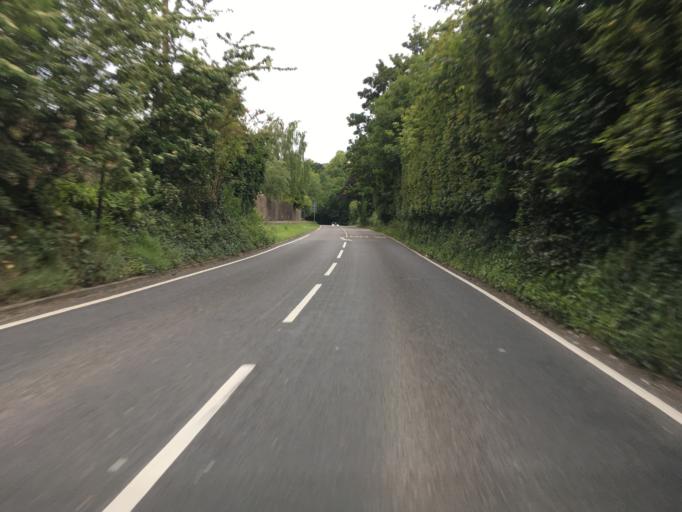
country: GB
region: England
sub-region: North Somerset
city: Long Ashton
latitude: 51.4608
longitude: -2.6613
